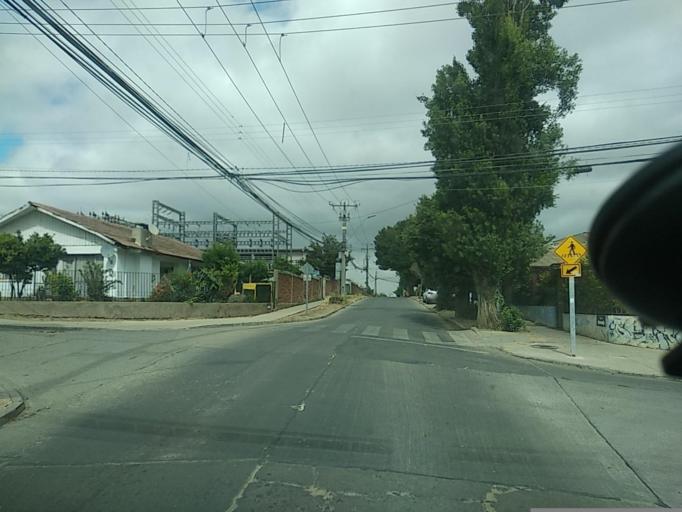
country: CL
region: Valparaiso
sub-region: Provincia de Marga Marga
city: Villa Alemana
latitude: -33.0420
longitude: -71.3705
